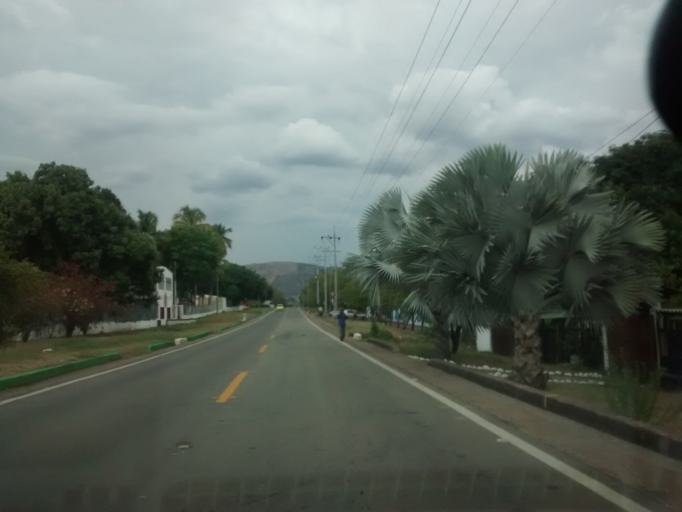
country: CO
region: Cundinamarca
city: Tocaima
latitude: 4.4479
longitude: -74.6580
